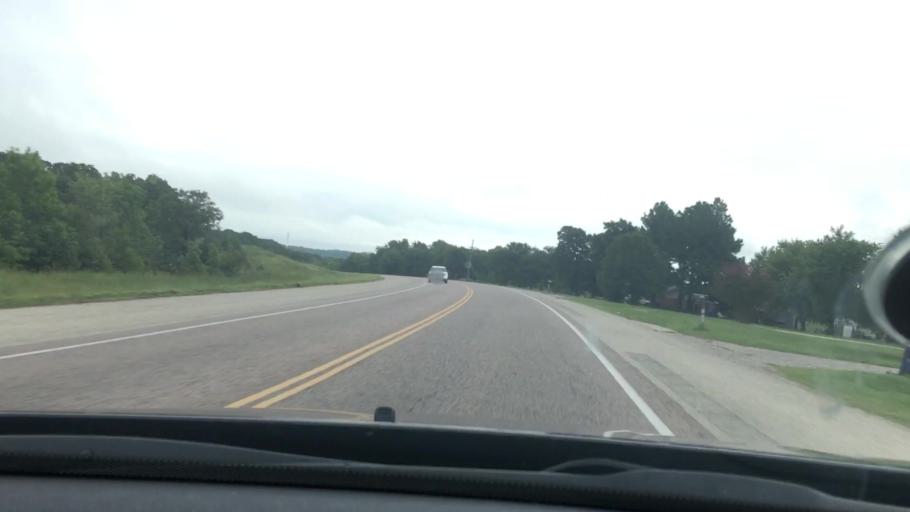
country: US
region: Oklahoma
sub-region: Pontotoc County
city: Ada
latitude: 34.7829
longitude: -96.5759
